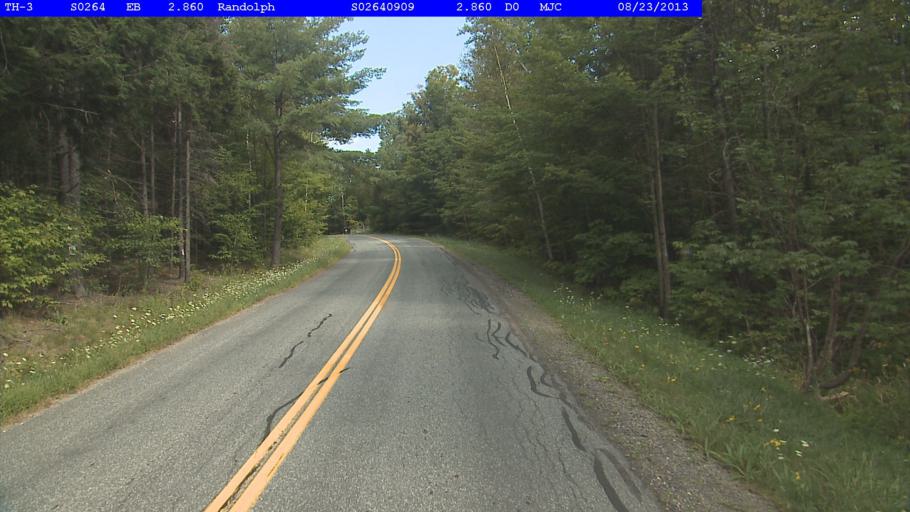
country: US
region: Vermont
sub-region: Orange County
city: Chelsea
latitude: 43.9639
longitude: -72.5227
